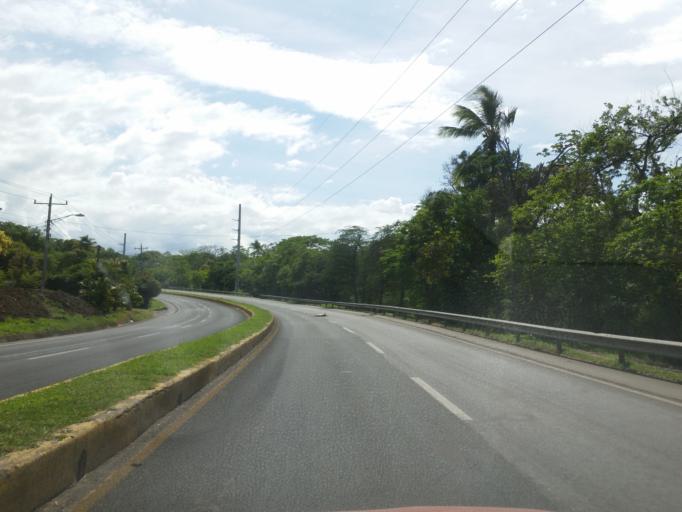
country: NI
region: Masaya
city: Masaya
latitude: 11.9784
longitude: -86.0509
